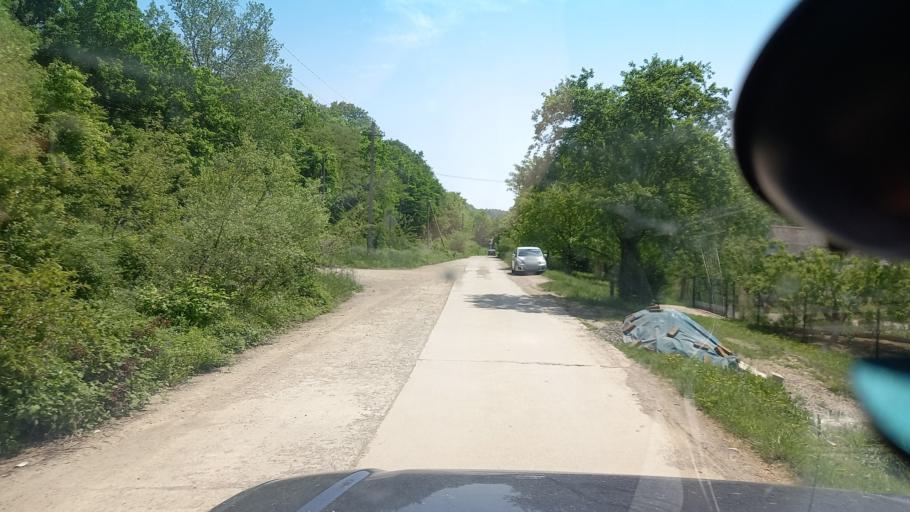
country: RU
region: Krasnodarskiy
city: Tuapse
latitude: 44.2474
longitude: 39.2389
